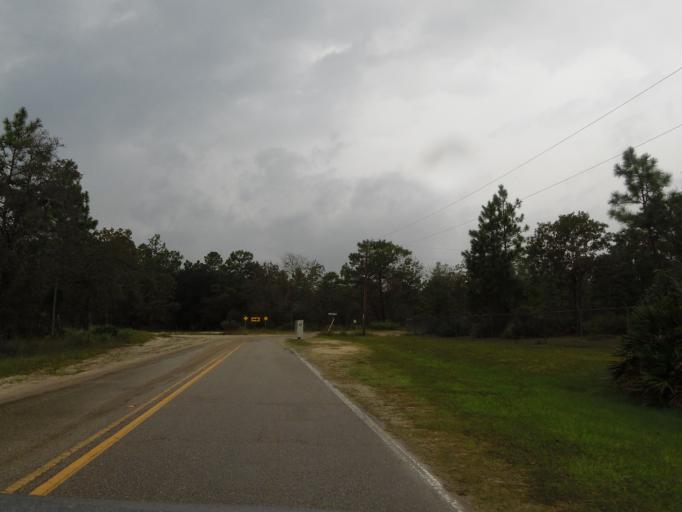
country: US
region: Florida
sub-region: Clay County
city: Middleburg
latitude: 30.1284
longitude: -81.9652
